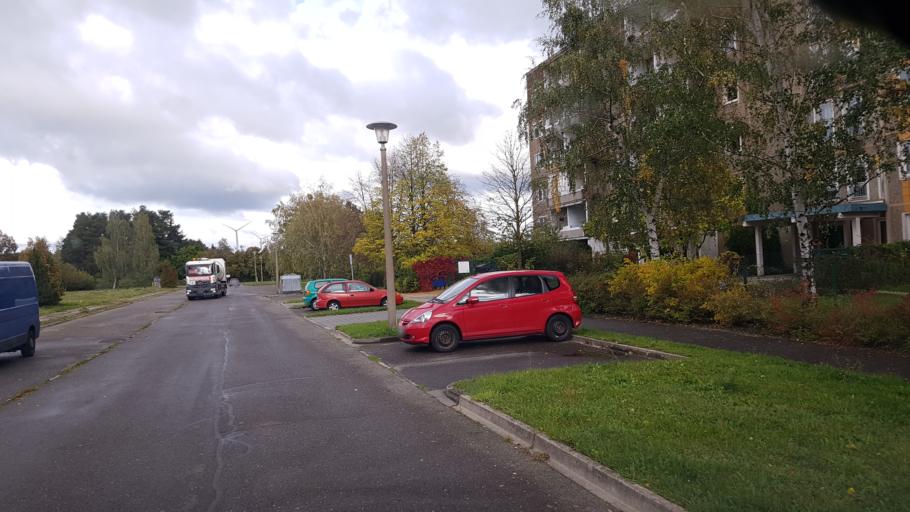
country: DE
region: Brandenburg
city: Grossraschen
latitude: 51.5980
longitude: 14.0004
